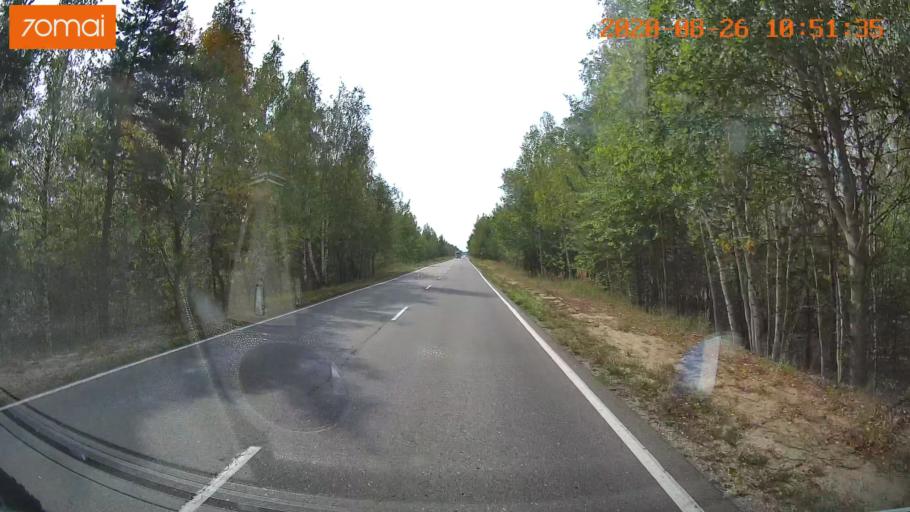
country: RU
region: Rjazan
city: Lashma
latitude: 54.6700
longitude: 41.1549
